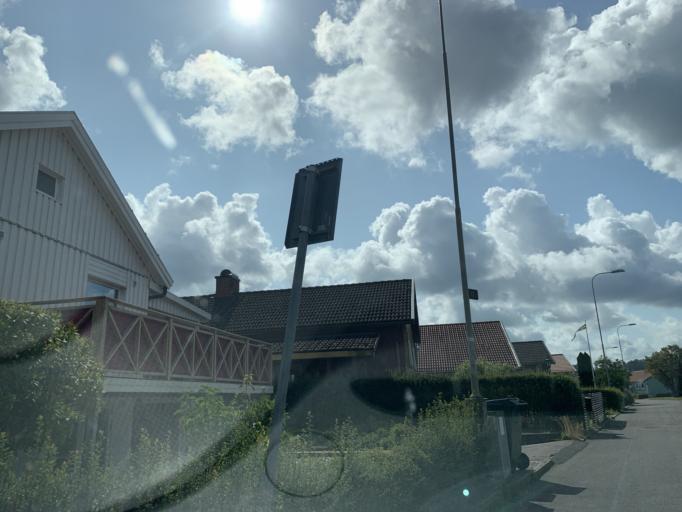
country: SE
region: Vaestra Goetaland
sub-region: Goteborg
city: Eriksbo
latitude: 57.7406
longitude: 12.0662
